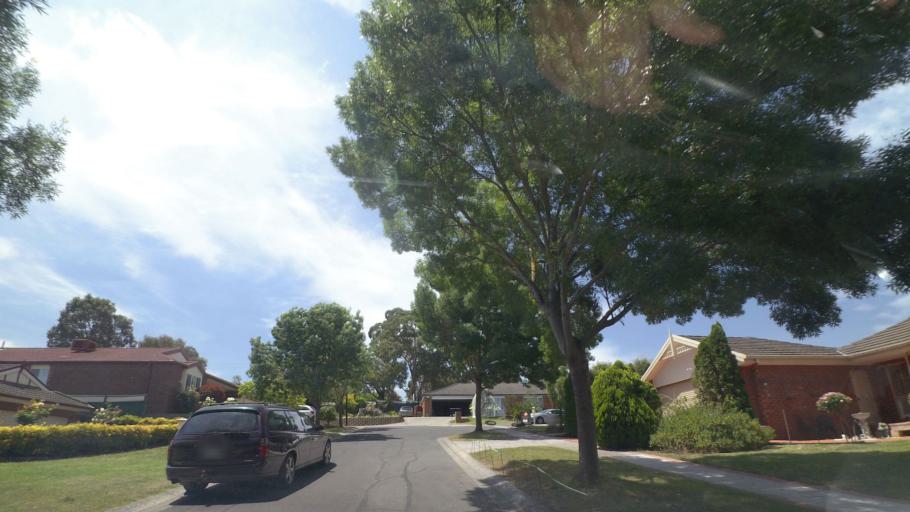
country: AU
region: Victoria
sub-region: Yarra Ranges
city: Chirnside Park
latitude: -37.7573
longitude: 145.3022
